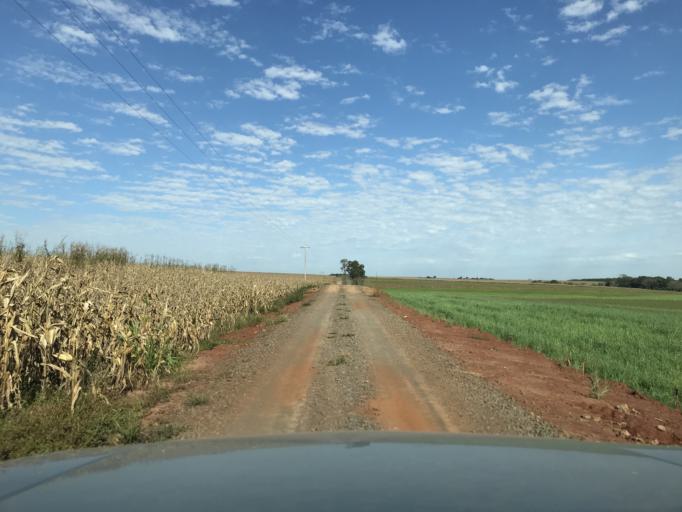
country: BR
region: Parana
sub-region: Palotina
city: Palotina
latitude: -24.1646
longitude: -53.7506
